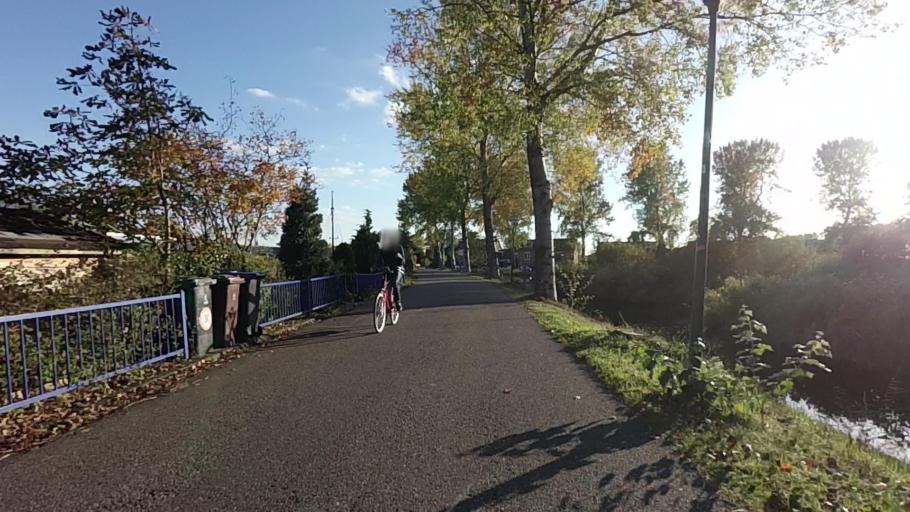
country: NL
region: North Holland
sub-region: Gemeente Amsterdam
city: Driemond
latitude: 52.2736
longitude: 5.0218
